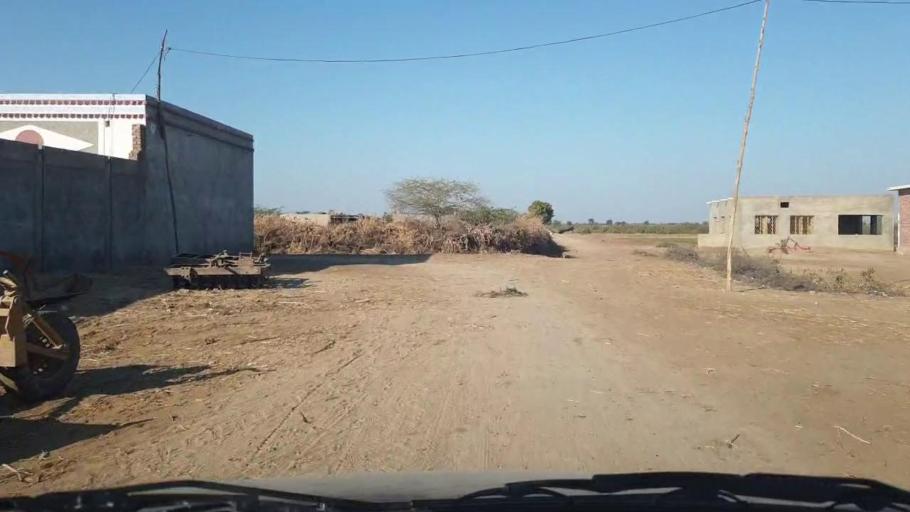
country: PK
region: Sindh
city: Samaro
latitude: 25.3622
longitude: 69.3025
